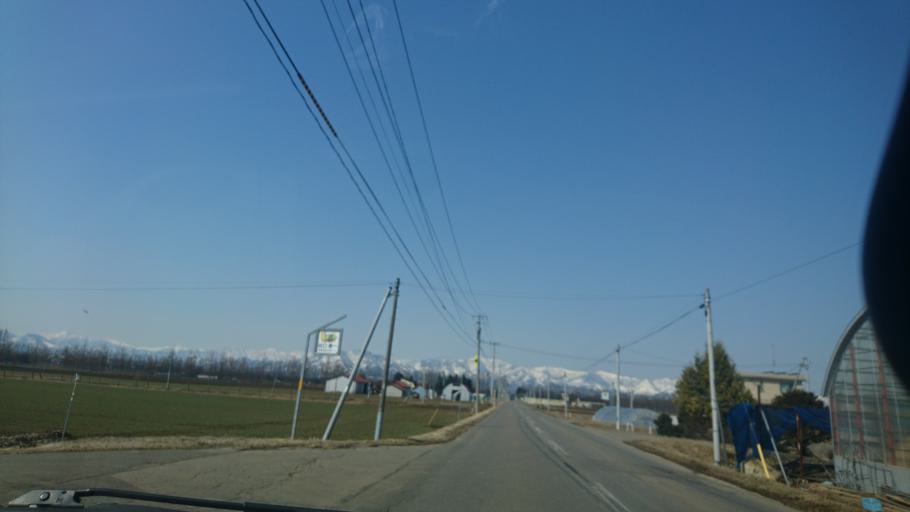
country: JP
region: Hokkaido
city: Obihiro
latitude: 42.9031
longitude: 143.0796
